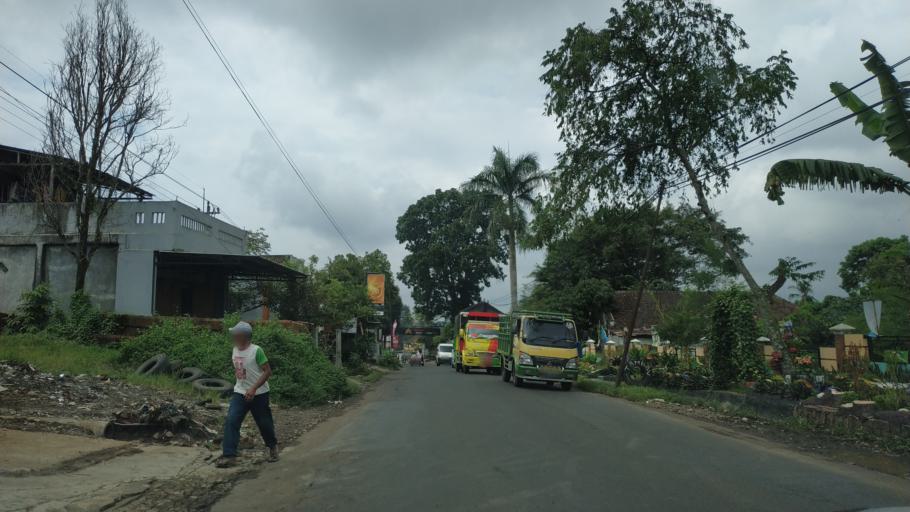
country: ID
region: Central Java
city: Weleri
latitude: -7.0913
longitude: 110.0513
